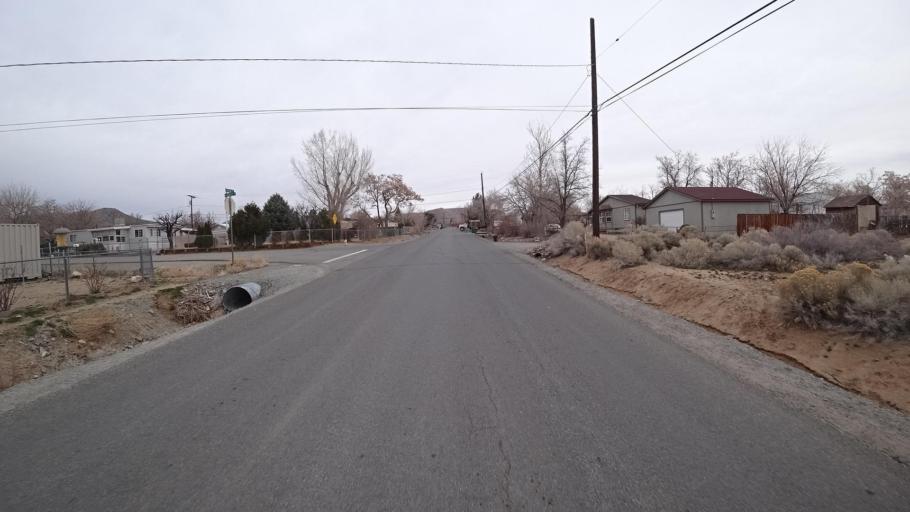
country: US
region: Nevada
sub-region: Washoe County
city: Sun Valley
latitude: 39.6047
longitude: -119.7710
